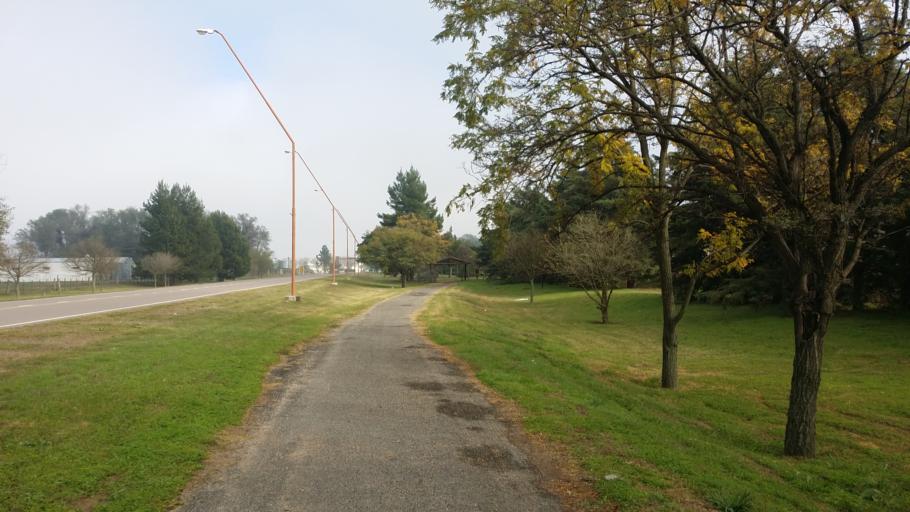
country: AR
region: La Pampa
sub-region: Departamento de Quemu Quemu
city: Quemu Quemu
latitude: -36.0639
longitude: -63.5836
